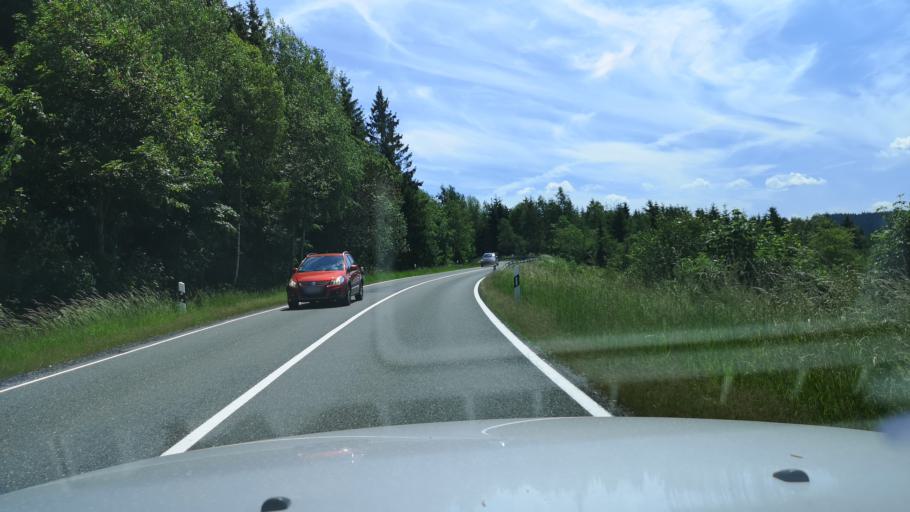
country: DE
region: Bavaria
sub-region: Upper Franconia
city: Tettau
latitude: 50.4912
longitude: 11.2607
